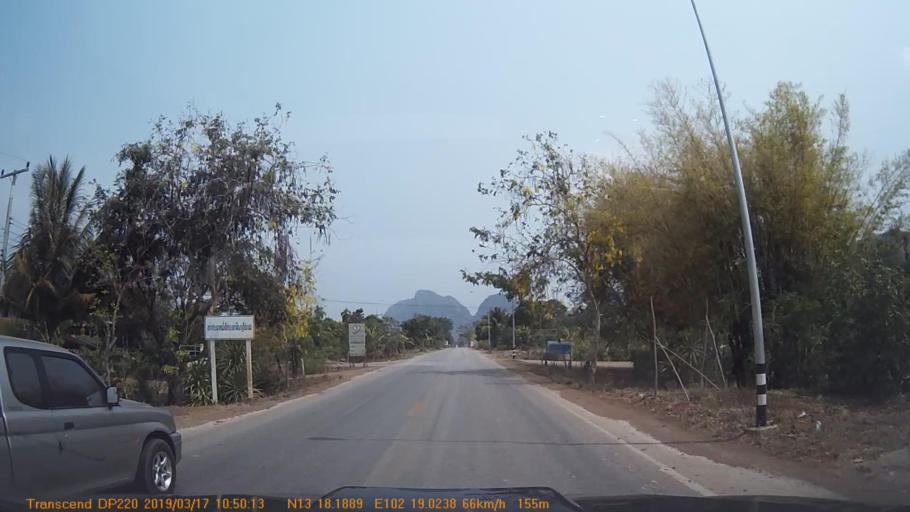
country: TH
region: Sa Kaeo
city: Wang Sombun
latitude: 13.3037
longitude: 102.3171
